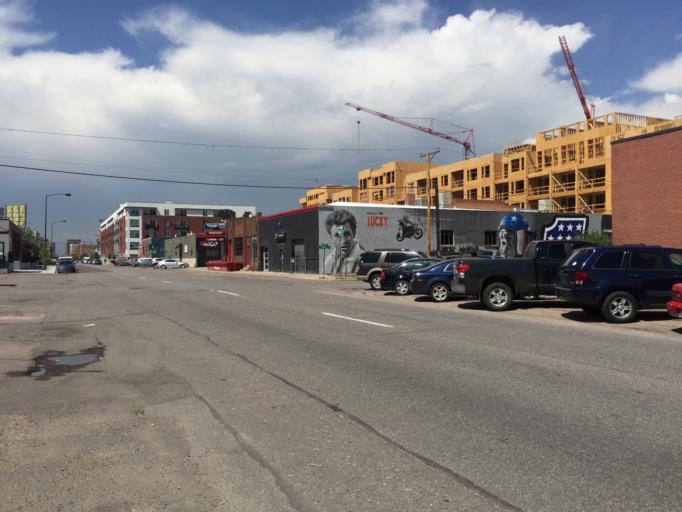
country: US
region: Colorado
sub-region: Denver County
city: Denver
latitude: 39.7624
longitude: -104.9822
